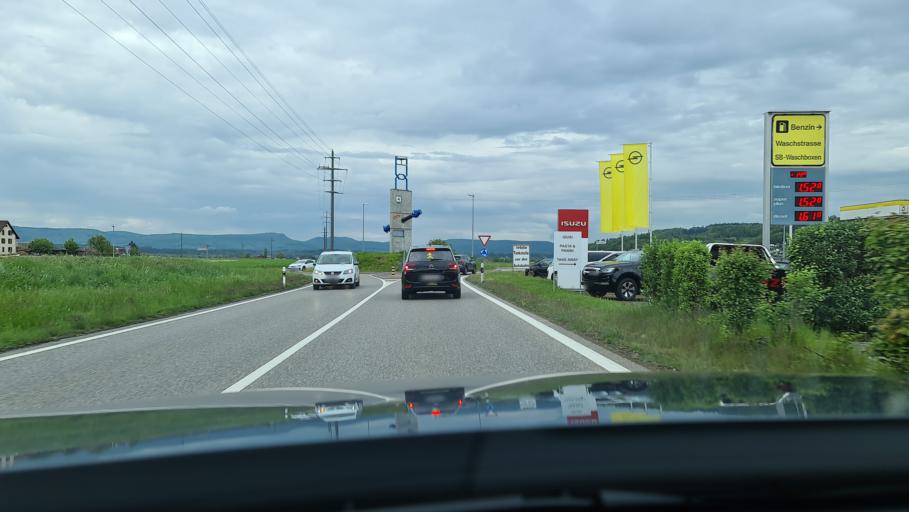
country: CH
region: Aargau
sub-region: Bezirk Kulm
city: Schoftland
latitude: 47.3192
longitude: 8.0471
